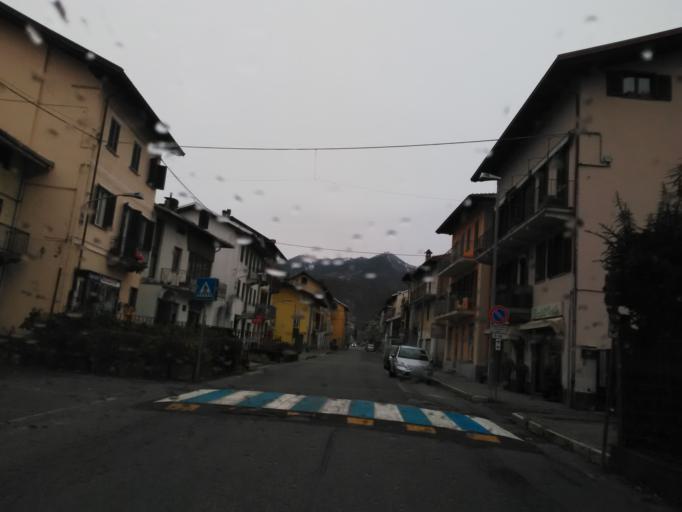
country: IT
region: Piedmont
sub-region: Provincia di Biella
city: Pray
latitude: 45.6754
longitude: 8.2134
